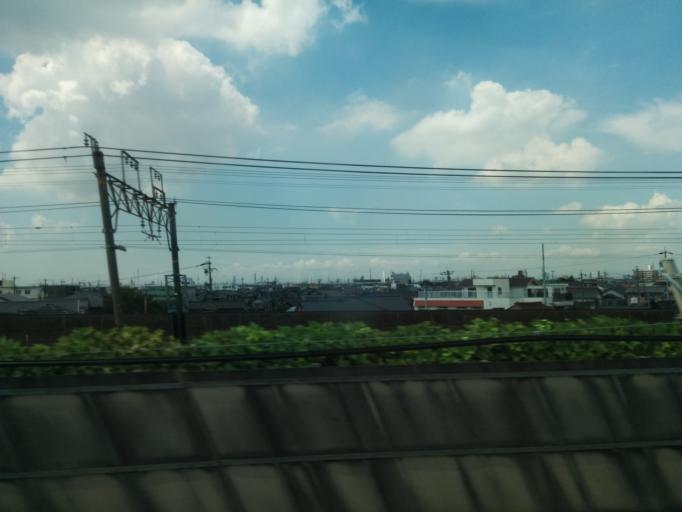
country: JP
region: Aichi
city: Obu
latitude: 35.0768
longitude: 136.9365
